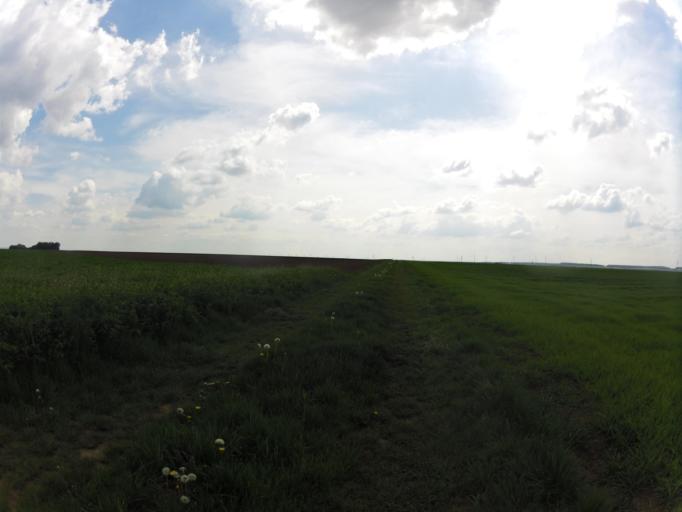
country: DE
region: Bavaria
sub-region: Regierungsbezirk Unterfranken
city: Sulzdorf
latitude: 49.6322
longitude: 9.9225
